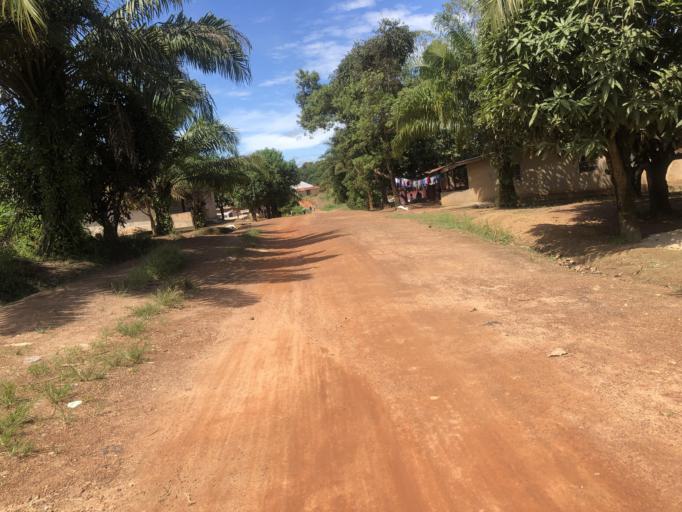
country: SL
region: Eastern Province
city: Koidu
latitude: 8.6400
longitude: -10.9512
